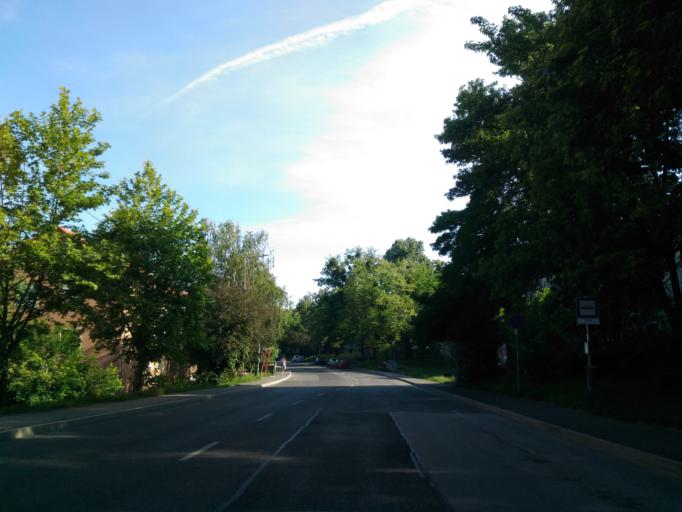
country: HU
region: Baranya
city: Komlo
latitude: 46.1815
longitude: 18.2595
